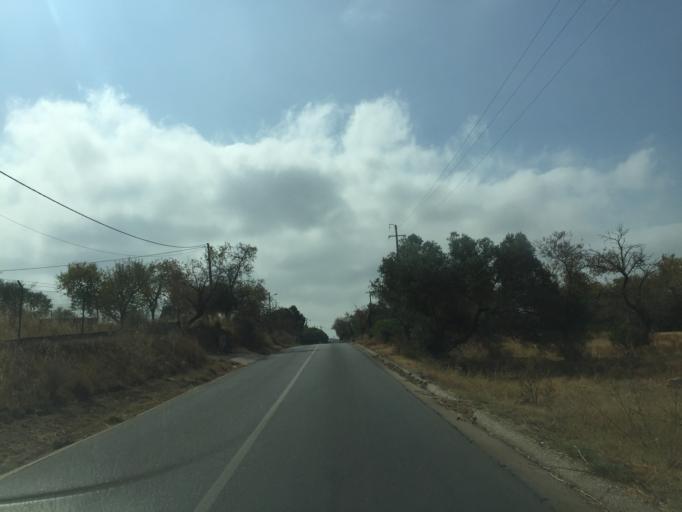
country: PT
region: Faro
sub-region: Olhao
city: Olhao
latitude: 37.0787
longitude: -7.8909
